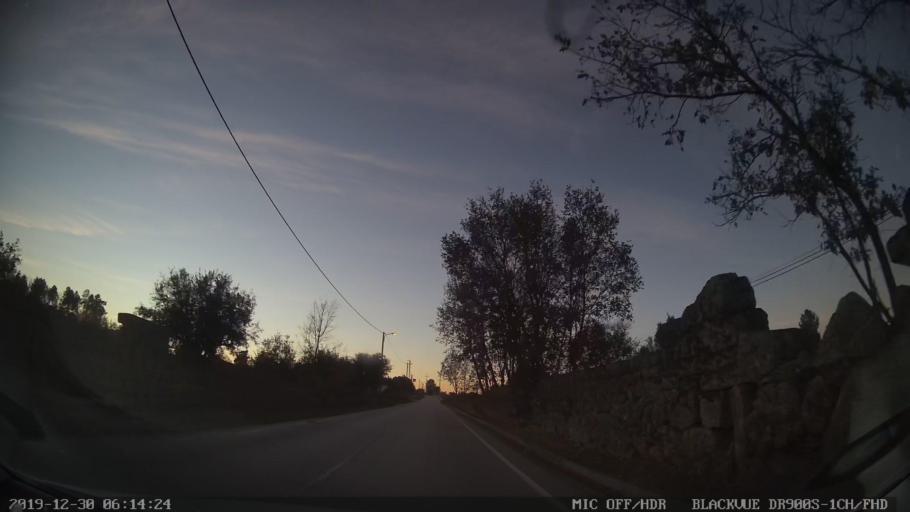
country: PT
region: Castelo Branco
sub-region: Penamacor
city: Penamacor
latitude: 40.1127
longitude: -7.2173
